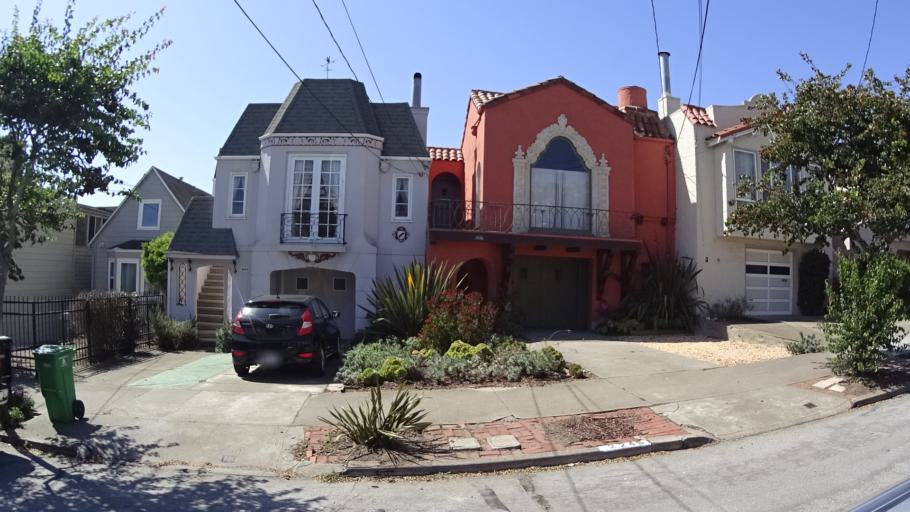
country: US
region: California
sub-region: San Mateo County
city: Daly City
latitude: 37.7461
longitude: -122.4738
